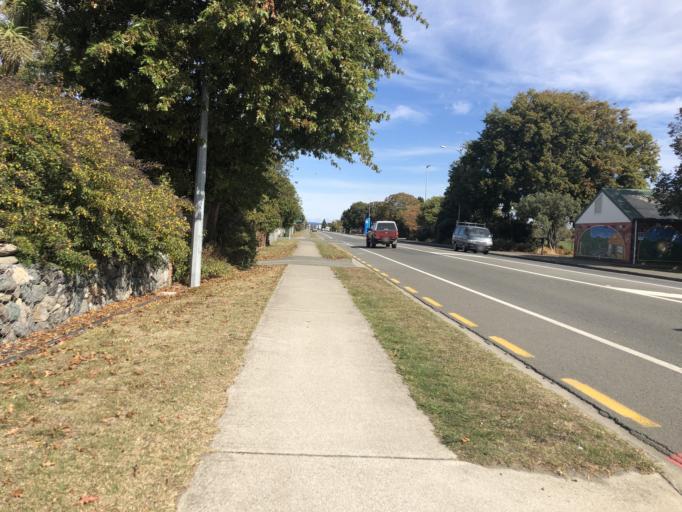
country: NZ
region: Tasman
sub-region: Tasman District
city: Richmond
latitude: -41.3386
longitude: 173.1788
